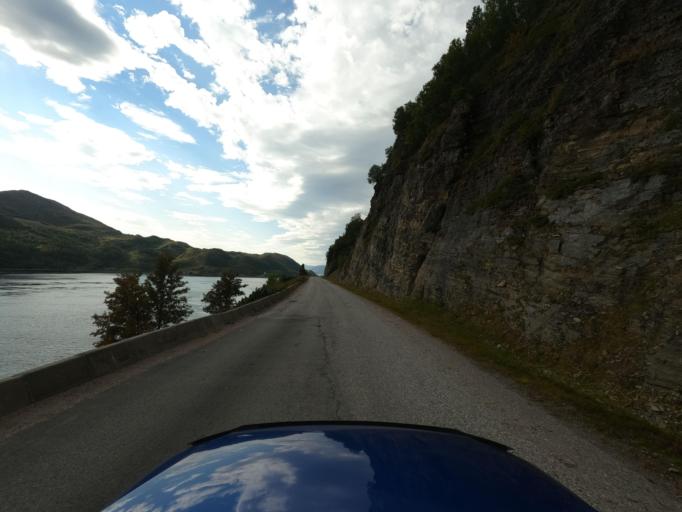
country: NO
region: Finnmark Fylke
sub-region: Kvalsund
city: Kvalsund
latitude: 70.5104
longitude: 23.9181
